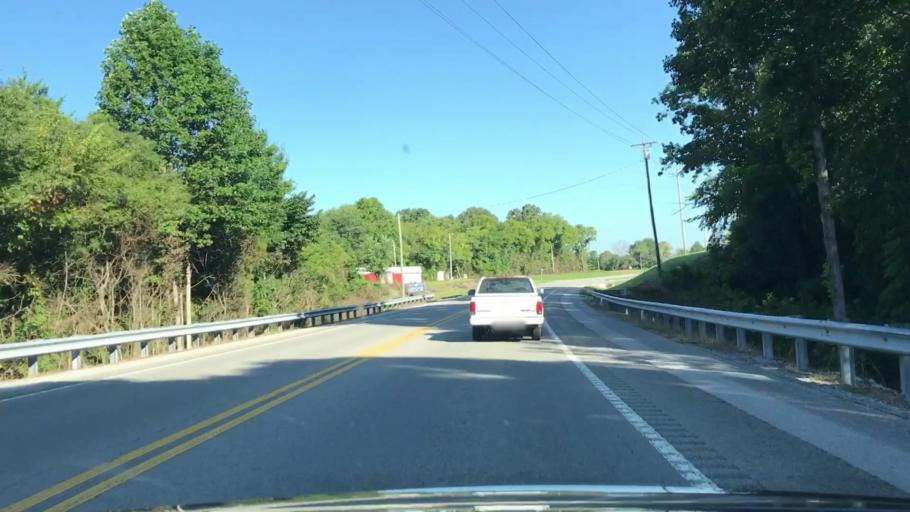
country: US
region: Tennessee
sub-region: Jackson County
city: Gainesboro
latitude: 36.2841
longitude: -85.6287
